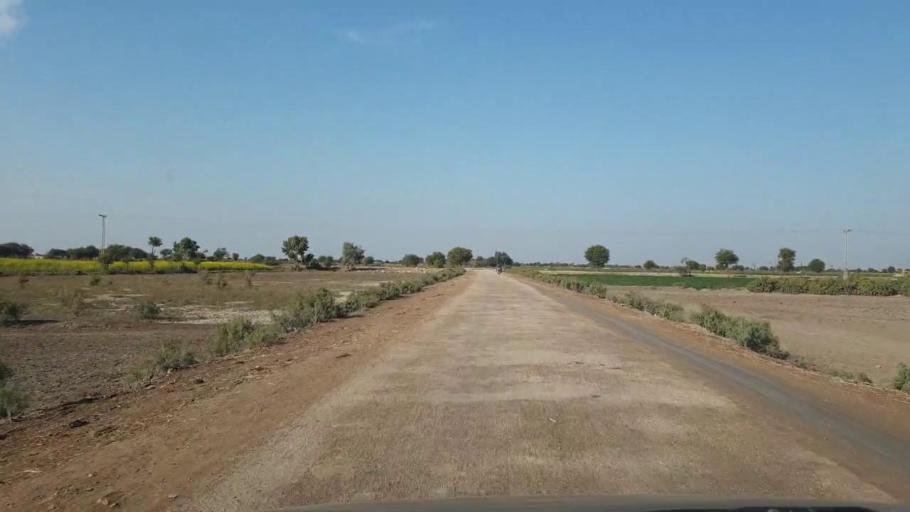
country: PK
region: Sindh
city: Khadro
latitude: 26.1656
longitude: 68.6865
